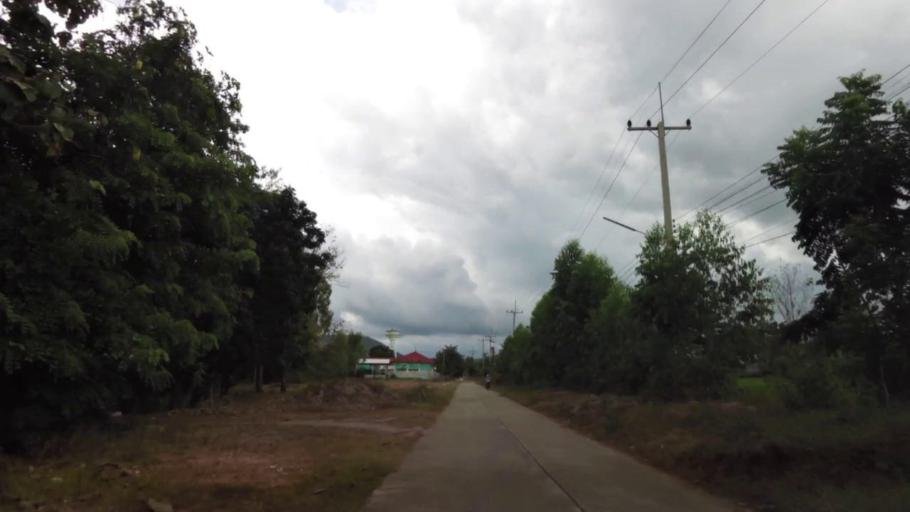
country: TH
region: Nakhon Sawan
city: Phai Sali
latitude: 15.6038
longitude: 100.6737
